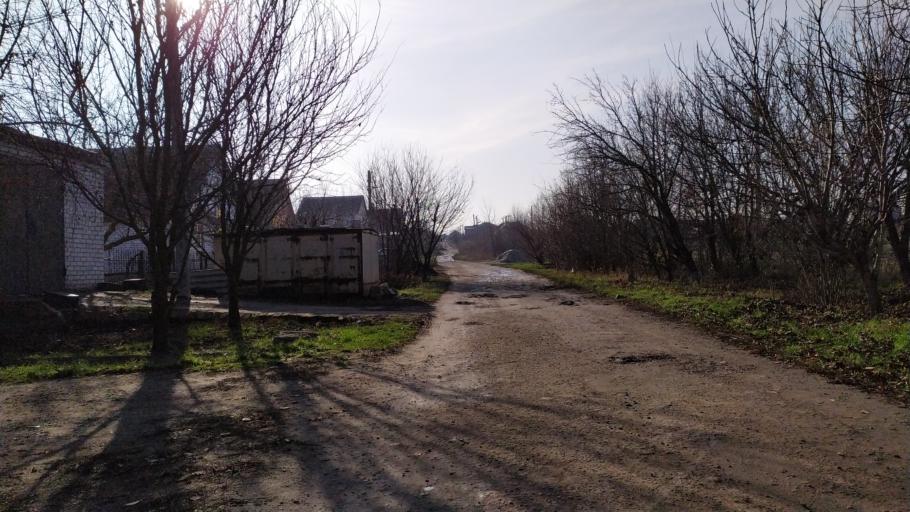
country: RU
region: Kursk
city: Kursk
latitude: 51.6400
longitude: 36.1301
